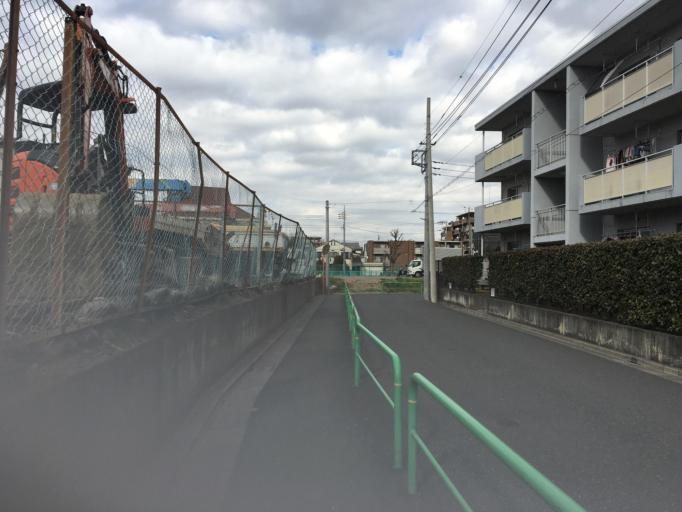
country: JP
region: Tokyo
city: Tokyo
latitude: 35.7471
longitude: 139.6694
